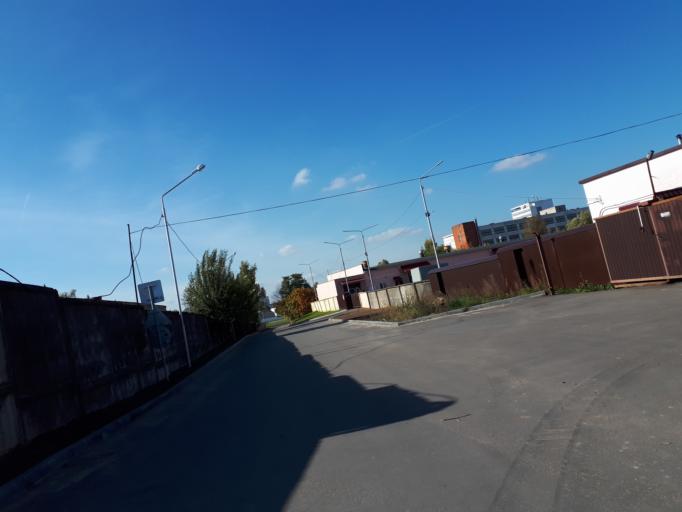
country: BY
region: Vitebsk
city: Vitebsk
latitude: 55.1638
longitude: 30.2439
